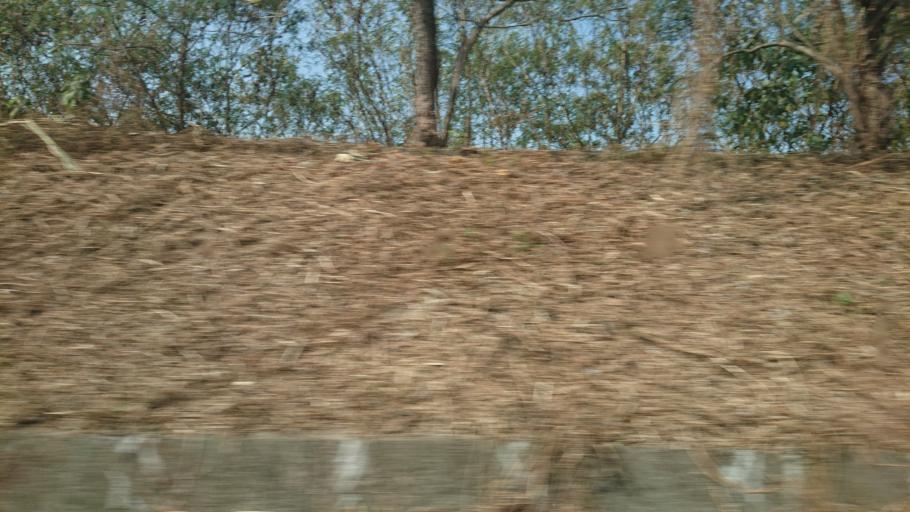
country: TW
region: Taiwan
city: Lugu
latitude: 23.7450
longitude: 120.6584
